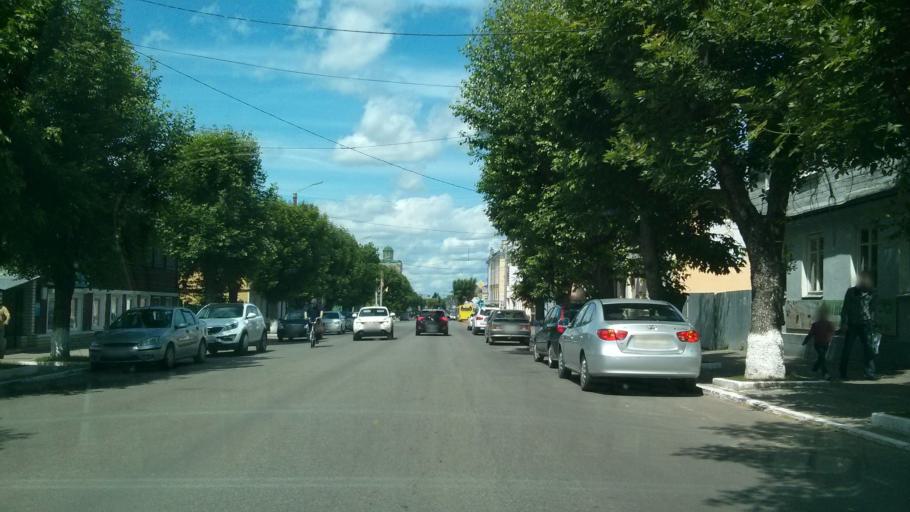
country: RU
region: Vladimir
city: Murom
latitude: 55.5757
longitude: 42.0549
